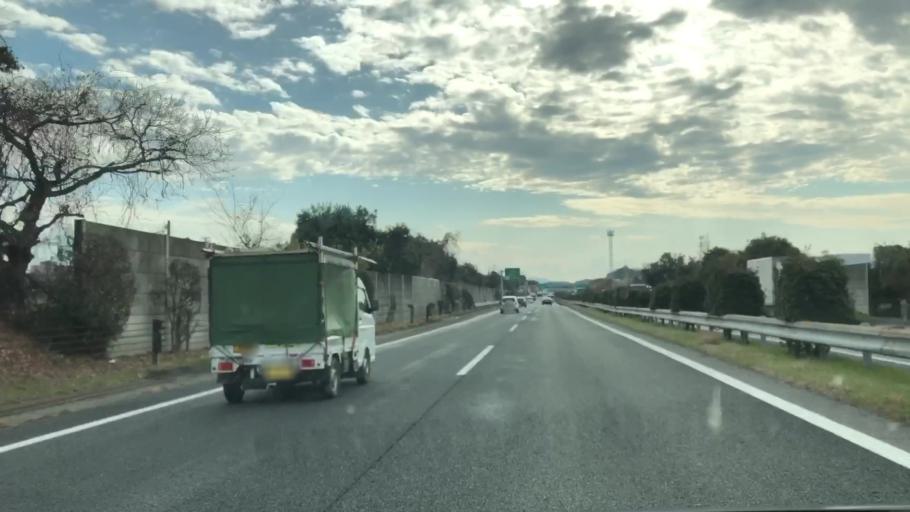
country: JP
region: Fukuoka
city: Kurume
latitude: 33.2633
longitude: 130.5385
